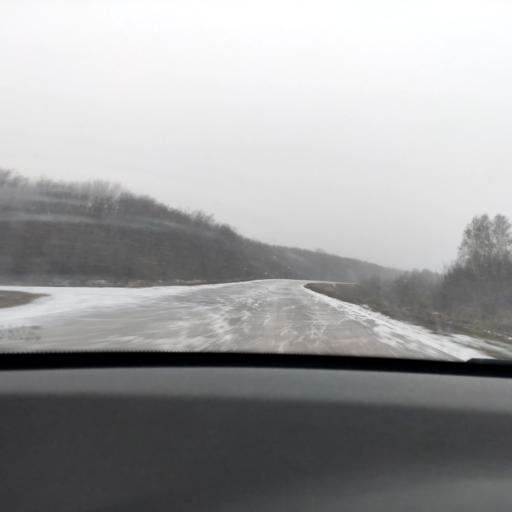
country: RU
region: Samara
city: Novokuybyshevsk
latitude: 52.9451
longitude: 49.8967
